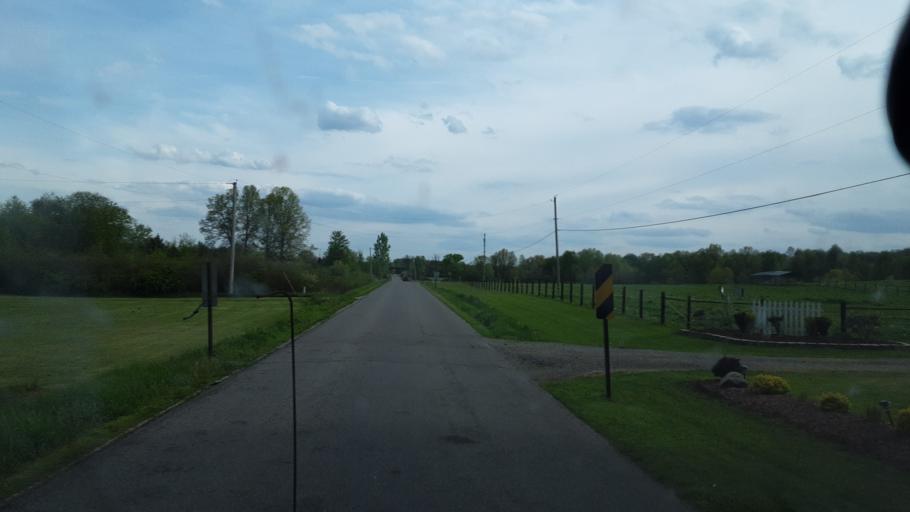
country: US
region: Ohio
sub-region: Portage County
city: Windham
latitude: 41.2483
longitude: -81.0666
